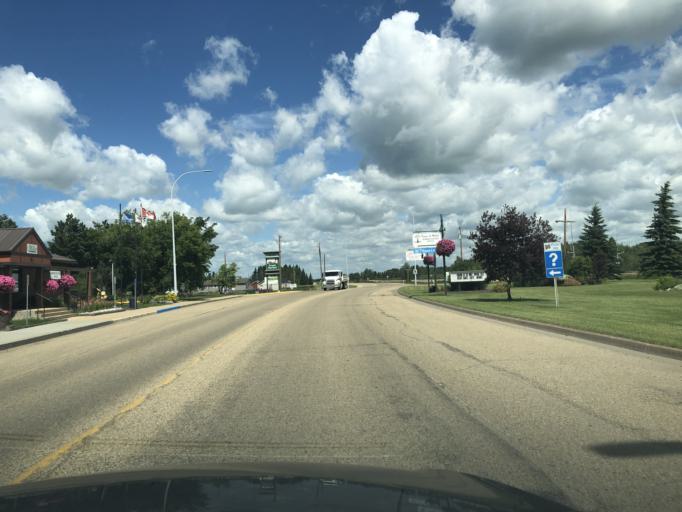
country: CA
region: Alberta
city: Millet
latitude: 53.0967
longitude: -113.4725
